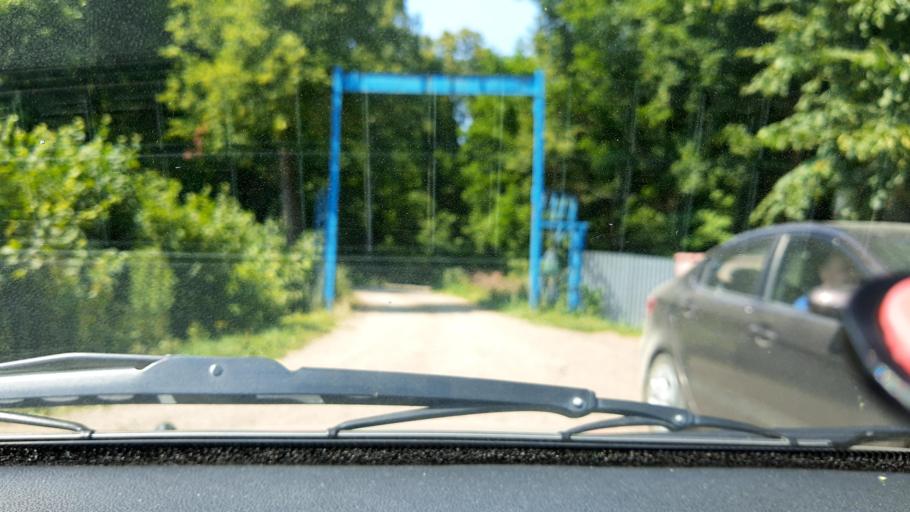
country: RU
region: Bashkortostan
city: Karmaskaly
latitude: 54.3820
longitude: 55.8971
